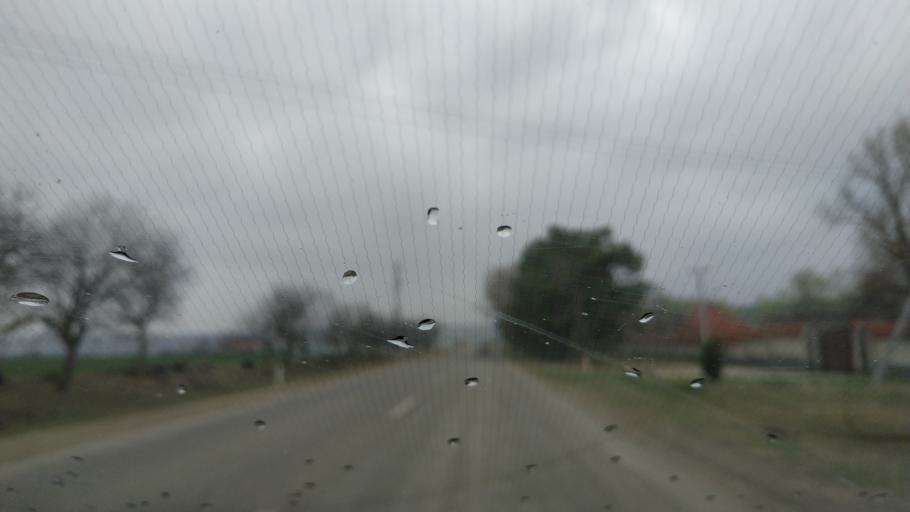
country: MD
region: Gagauzia
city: Comrat
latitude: 46.2466
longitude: 28.7620
